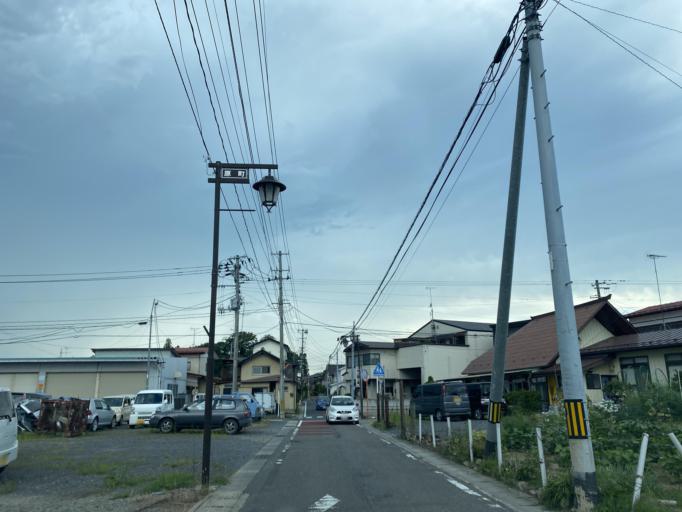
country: JP
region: Fukushima
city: Koriyama
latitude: 37.4458
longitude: 140.3939
